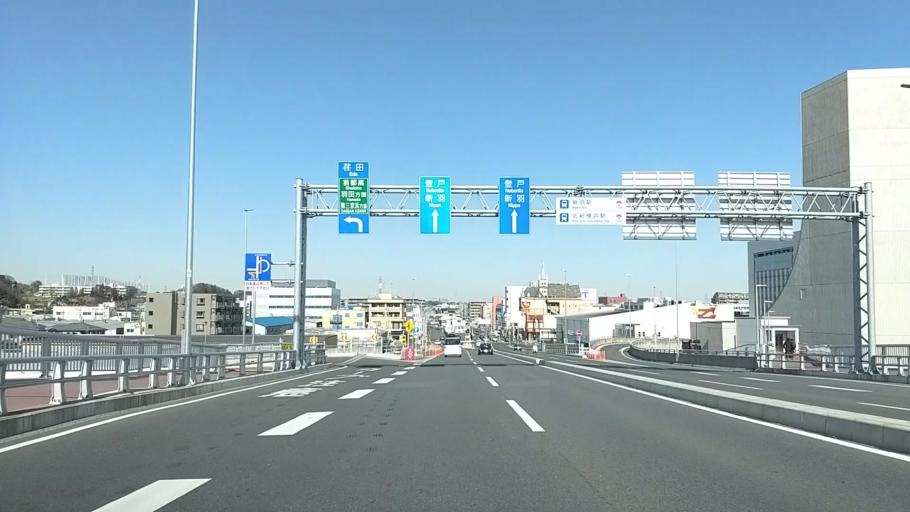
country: JP
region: Kanagawa
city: Yokohama
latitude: 35.5142
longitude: 139.6130
